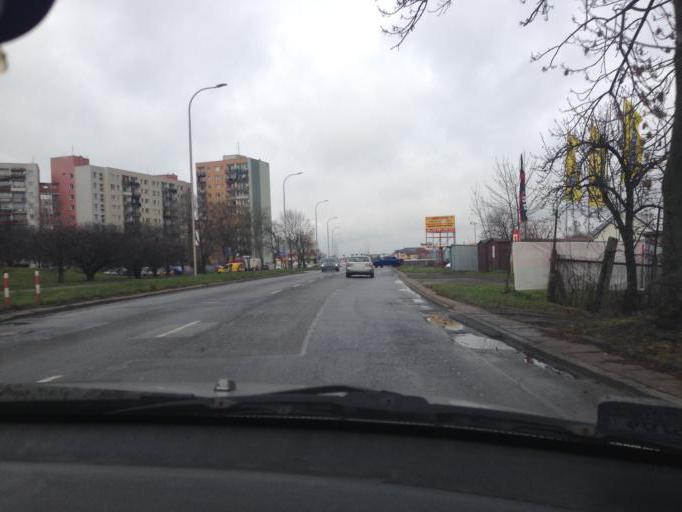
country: PL
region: Opole Voivodeship
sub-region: Powiat opolski
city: Opole
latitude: 50.6835
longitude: 17.9540
